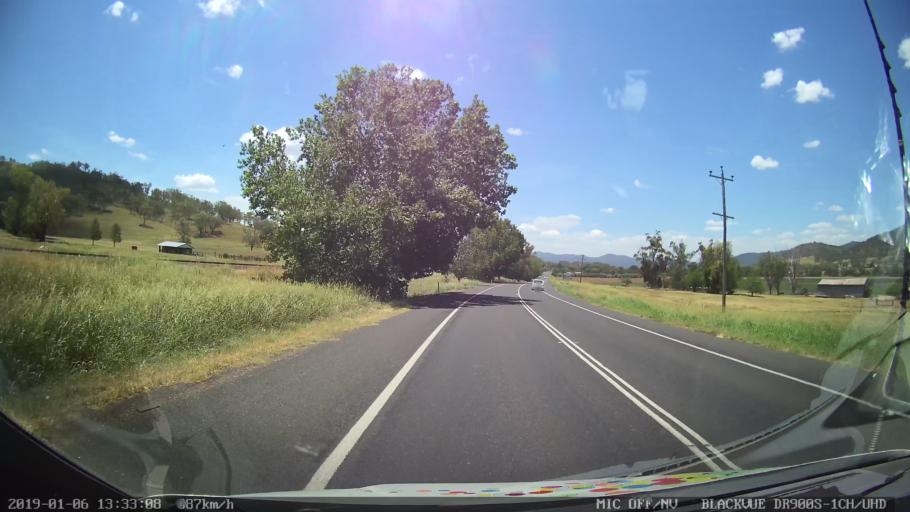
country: AU
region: New South Wales
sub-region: Tamworth Municipality
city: Kootingal
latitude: -31.1022
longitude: 151.0028
